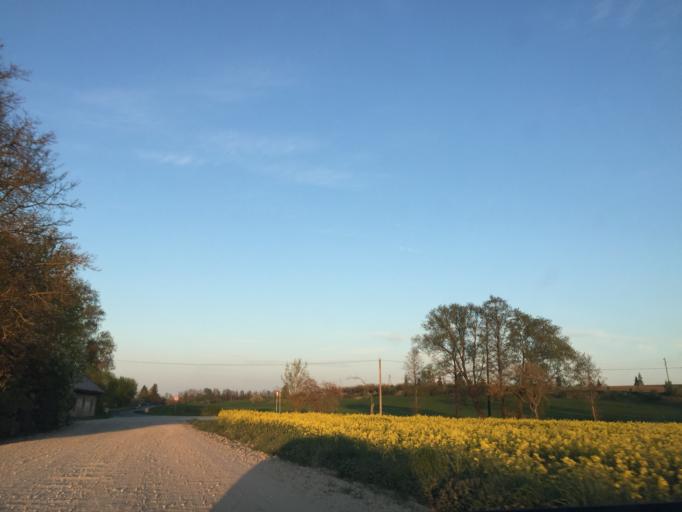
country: LV
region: Bauskas Rajons
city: Bauska
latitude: 56.4028
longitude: 24.1333
